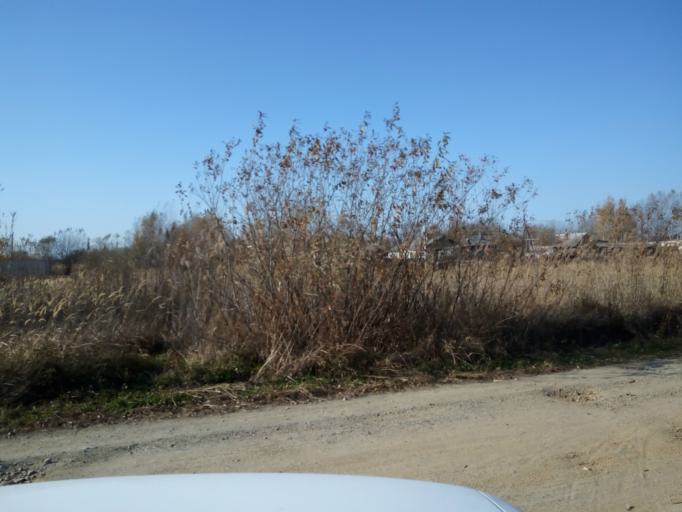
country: RU
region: Primorskiy
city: Dal'nerechensk
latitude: 45.9189
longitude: 133.7473
